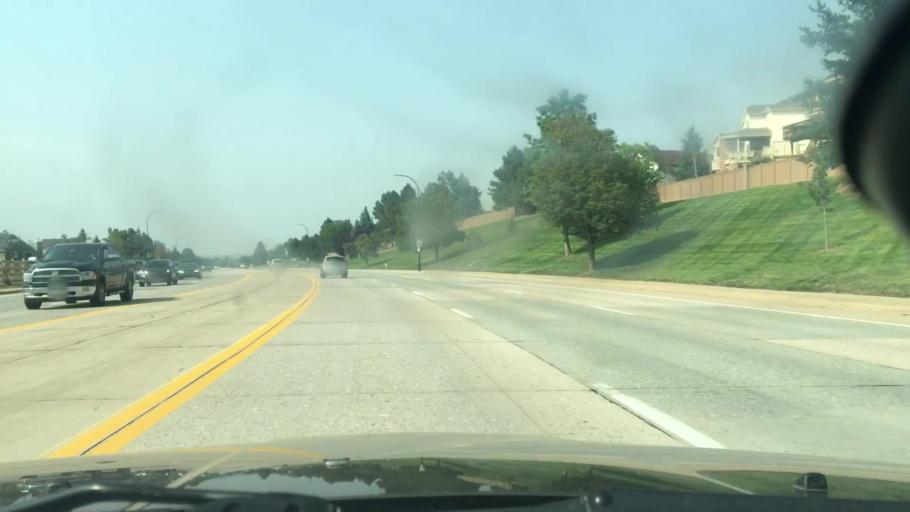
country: US
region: Colorado
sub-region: Douglas County
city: Acres Green
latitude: 39.5471
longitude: -104.9100
